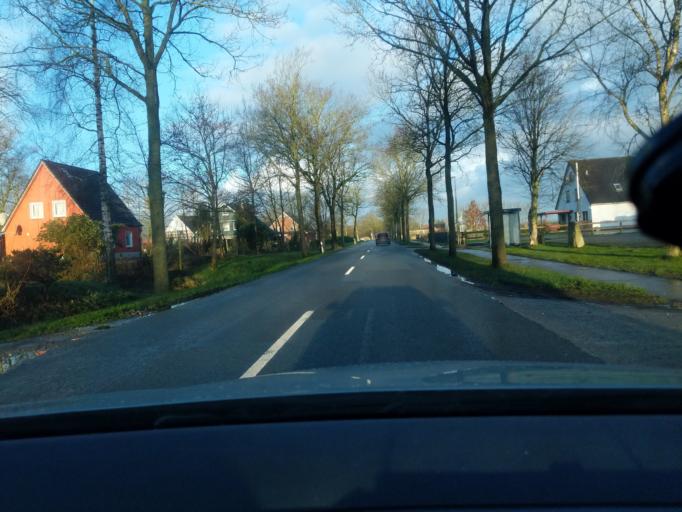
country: DE
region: Lower Saxony
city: Cuxhaven
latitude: 53.8229
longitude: 8.7494
